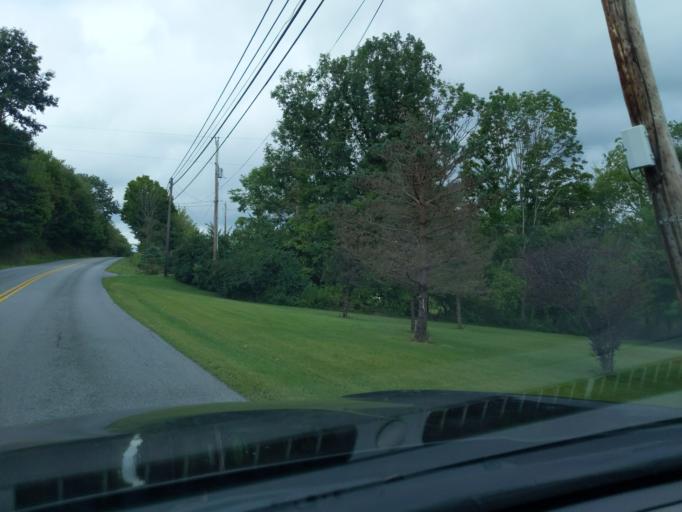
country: US
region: Pennsylvania
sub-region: Blair County
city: Roaring Spring
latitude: 40.3555
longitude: -78.4363
